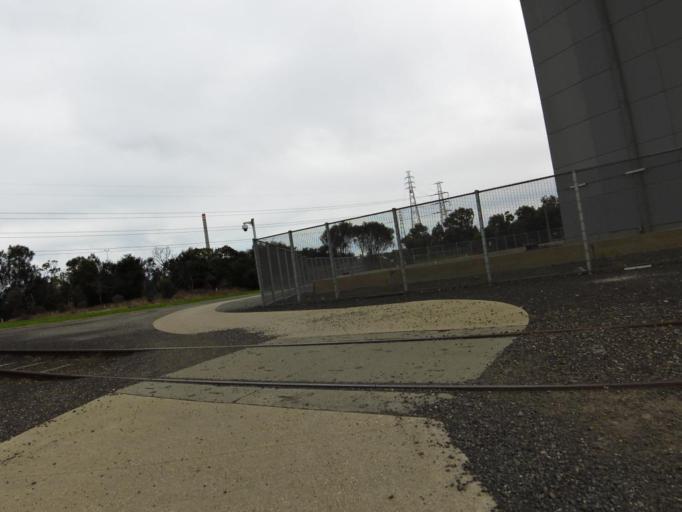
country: AU
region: Victoria
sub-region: Maribyrnong
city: Yarraville
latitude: -37.8328
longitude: 144.9045
